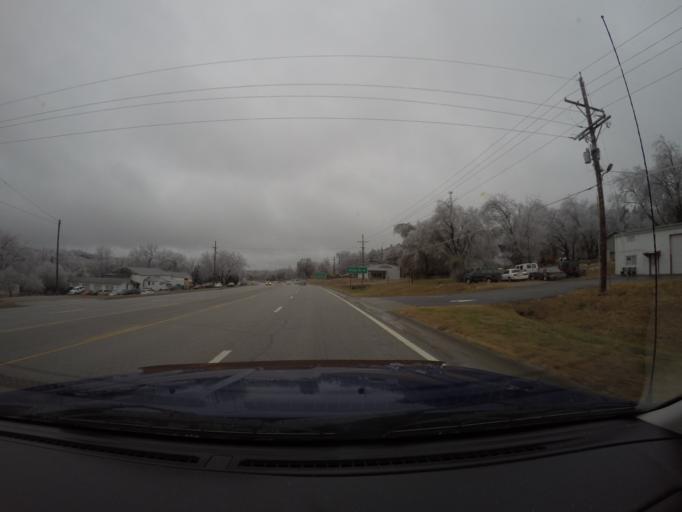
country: US
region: Kansas
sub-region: Riley County
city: Manhattan
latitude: 39.1696
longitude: -96.5421
